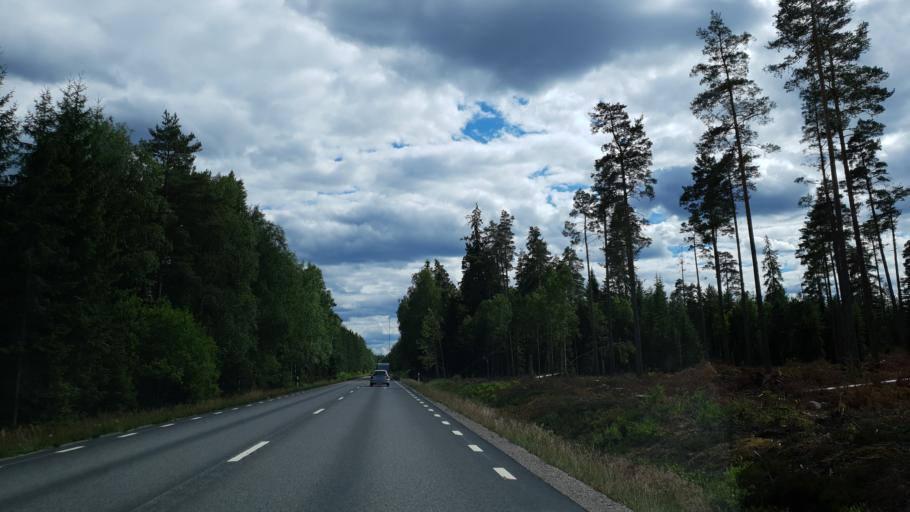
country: SE
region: Kronoberg
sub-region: Lessebo Kommun
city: Lessebo
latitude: 56.7875
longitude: 15.4141
